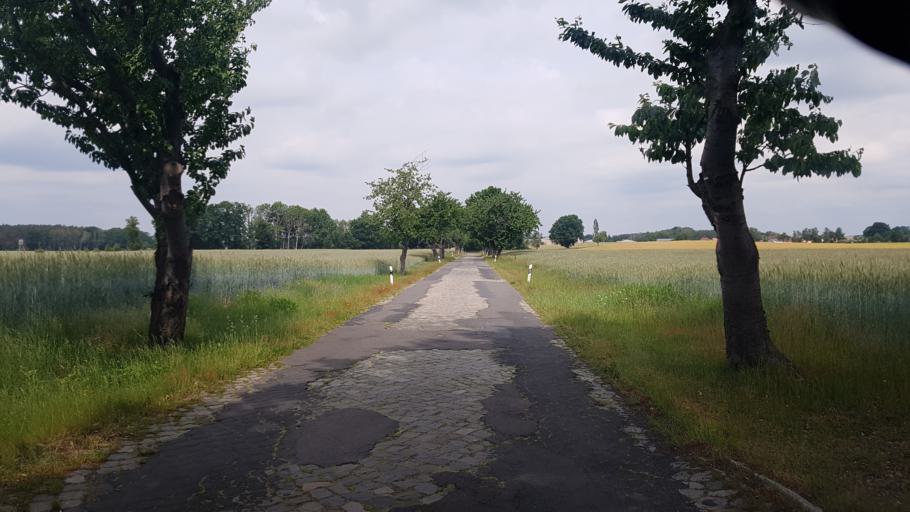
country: DE
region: Brandenburg
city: Lebusa
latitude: 51.8064
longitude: 13.4479
